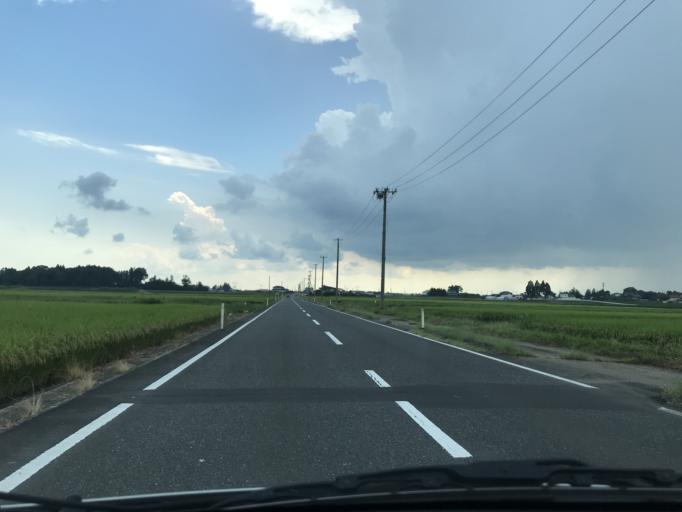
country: JP
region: Iwate
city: Ichinoseki
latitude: 38.7673
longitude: 141.0695
